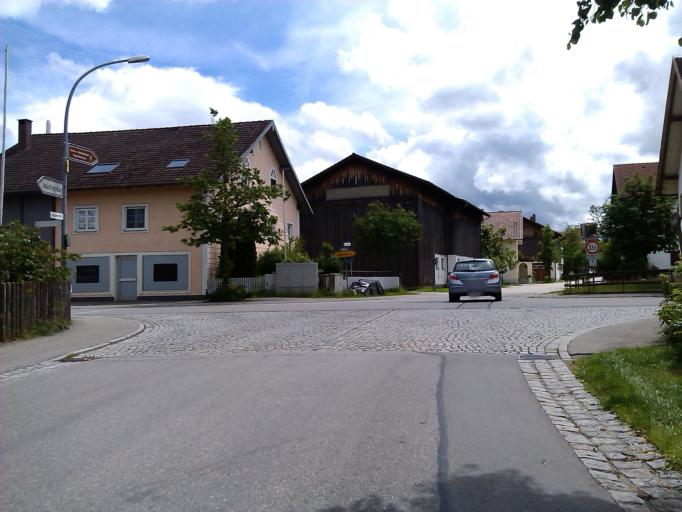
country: DE
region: Bavaria
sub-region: Swabia
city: Biessenhofen
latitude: 47.8170
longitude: 10.6215
